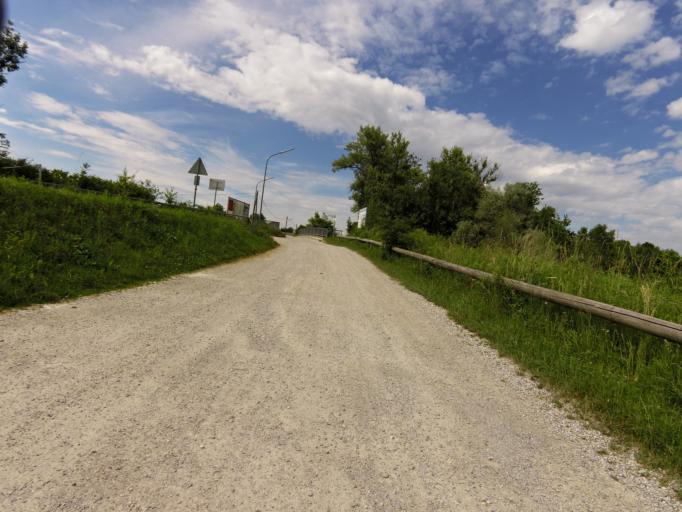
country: DE
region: Bavaria
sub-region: Upper Bavaria
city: Moosburg
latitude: 48.4598
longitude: 11.9451
